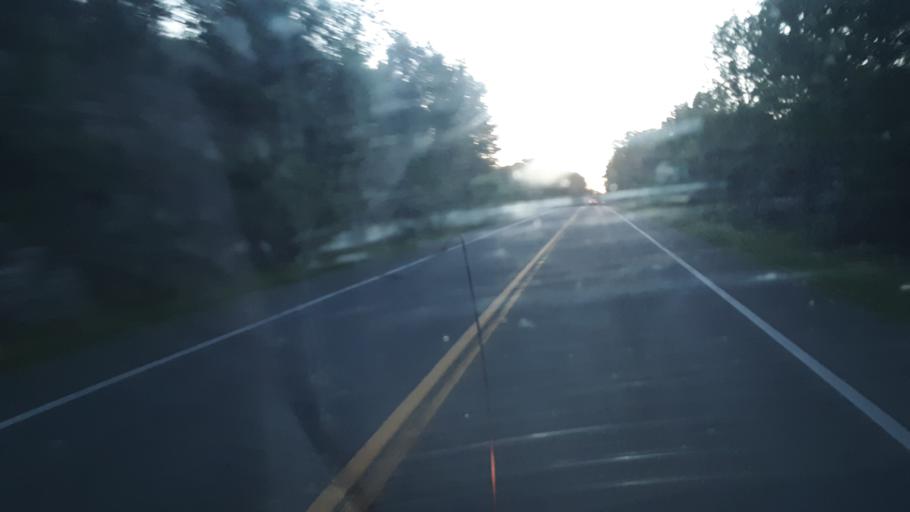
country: US
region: New York
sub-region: Montgomery County
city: Hagaman
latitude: 42.9726
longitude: -74.0724
